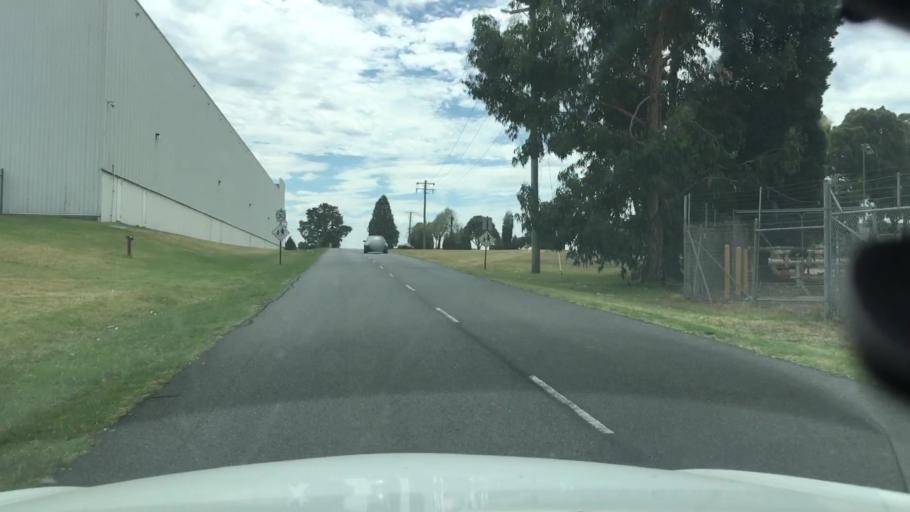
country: AU
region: Victoria
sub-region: Knox
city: Scoresby
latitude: -37.9037
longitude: 145.2263
